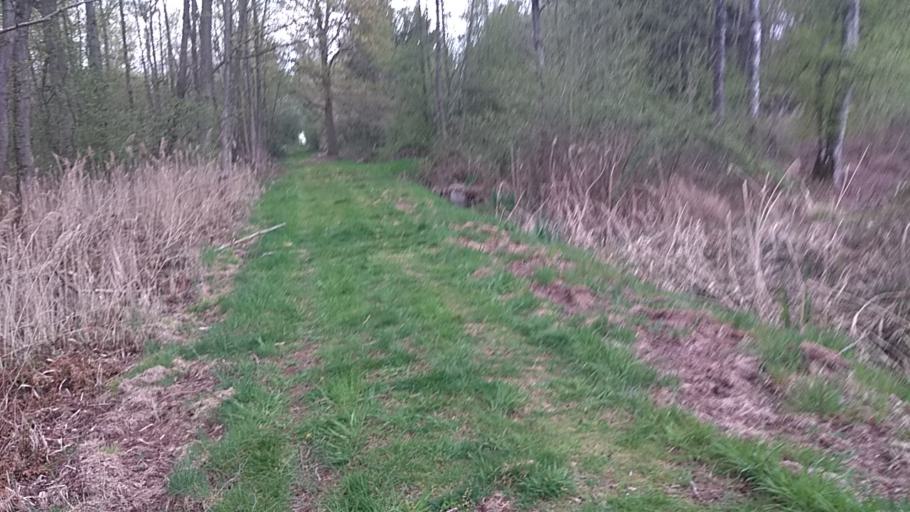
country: NL
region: Limburg
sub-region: Gemeente Leudal
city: Heythuysen
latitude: 51.2990
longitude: 5.8386
